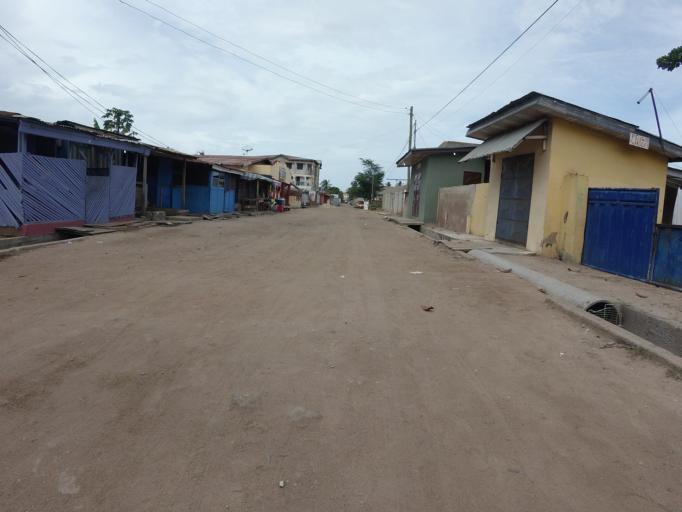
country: GH
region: Greater Accra
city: Accra
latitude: 5.5979
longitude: -0.2157
